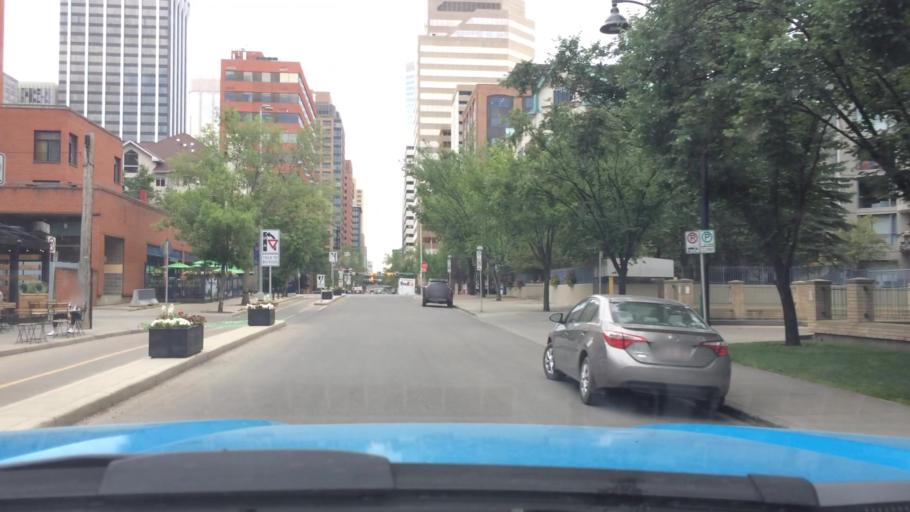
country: CA
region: Alberta
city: Calgary
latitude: 51.0515
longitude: -114.0785
